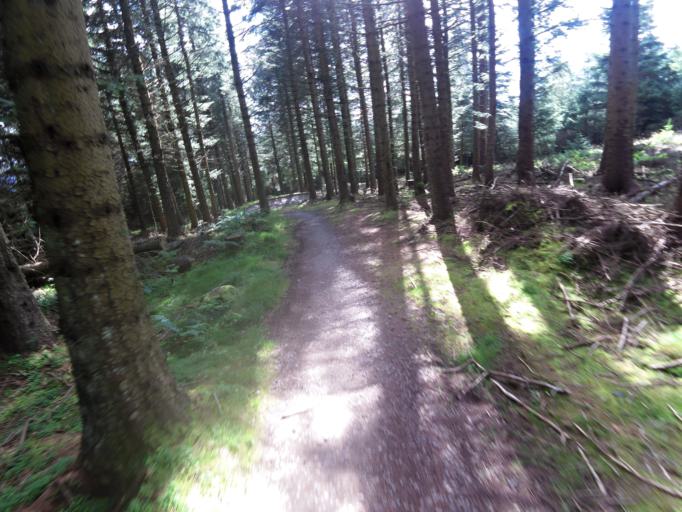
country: GB
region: Scotland
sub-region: The Scottish Borders
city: Peebles
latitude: 55.6668
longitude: -3.1276
